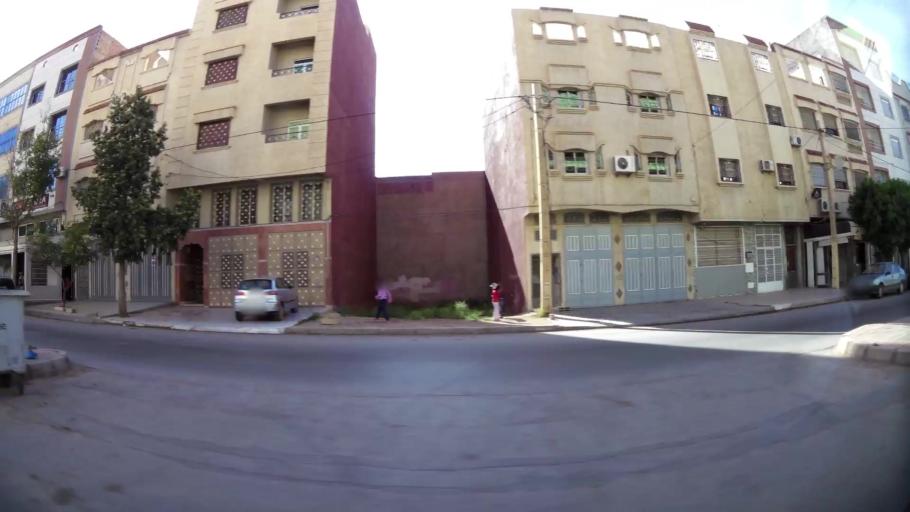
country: MA
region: Oriental
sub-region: Oujda-Angad
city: Oujda
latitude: 34.6690
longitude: -1.8952
